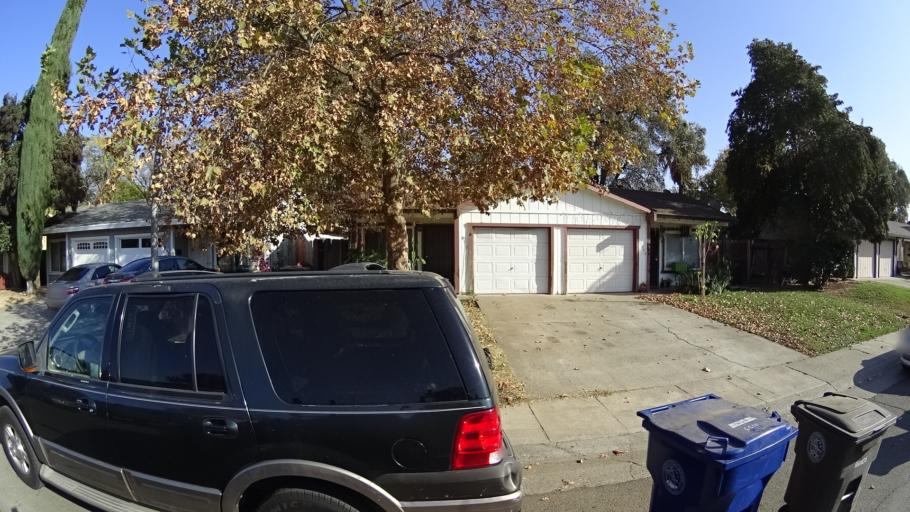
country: US
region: California
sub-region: Sacramento County
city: Citrus Heights
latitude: 38.6829
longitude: -121.2768
